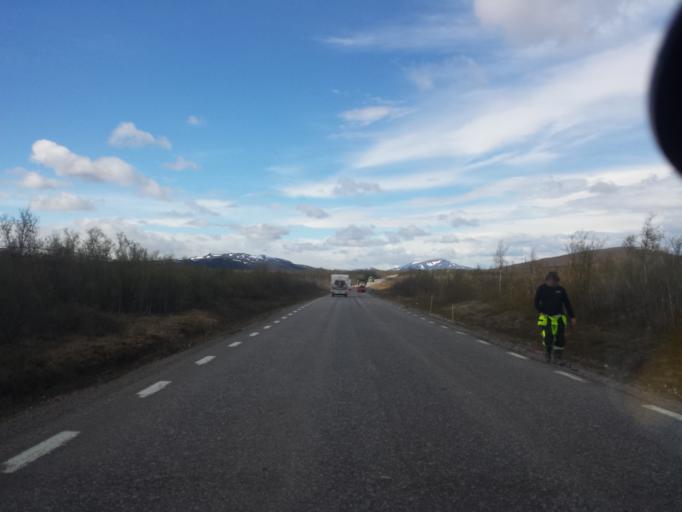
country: SE
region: Norrbotten
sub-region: Kiruna Kommun
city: Kiruna
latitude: 68.0116
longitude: 19.8434
